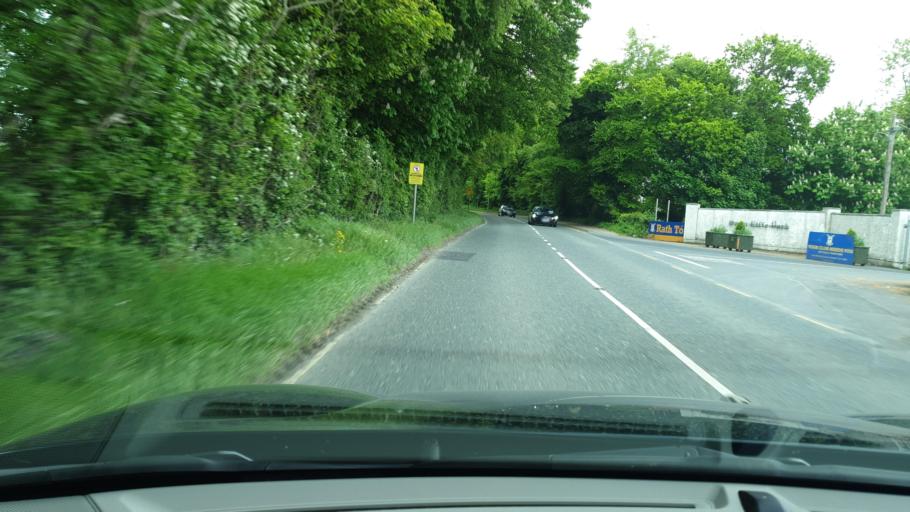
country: IE
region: Leinster
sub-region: An Mhi
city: Ratoath
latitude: 53.5113
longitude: -6.4773
